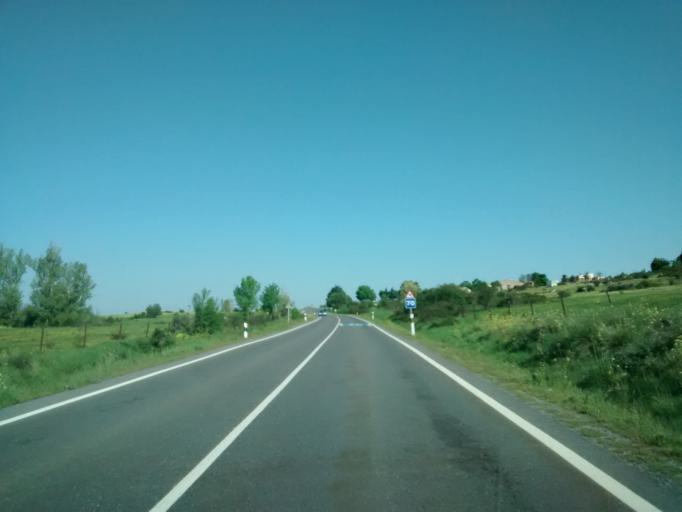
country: ES
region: Castille and Leon
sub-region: Provincia de Segovia
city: San Ildefonso
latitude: 40.9209
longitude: -4.0224
